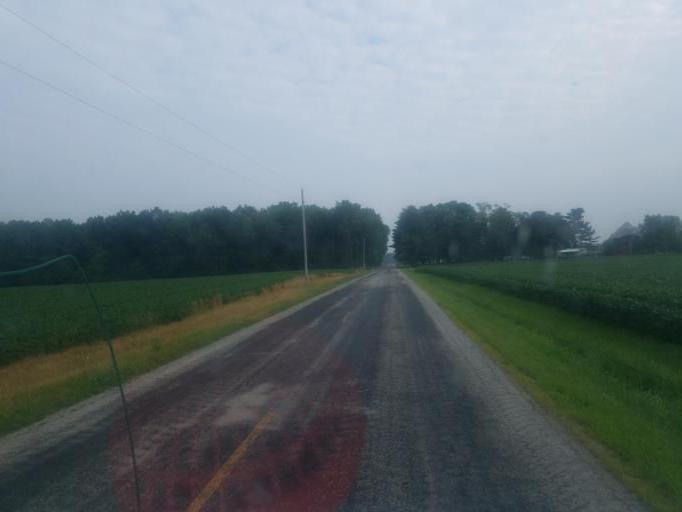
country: US
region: Ohio
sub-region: Morrow County
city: Cardington
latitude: 40.5770
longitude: -82.9766
